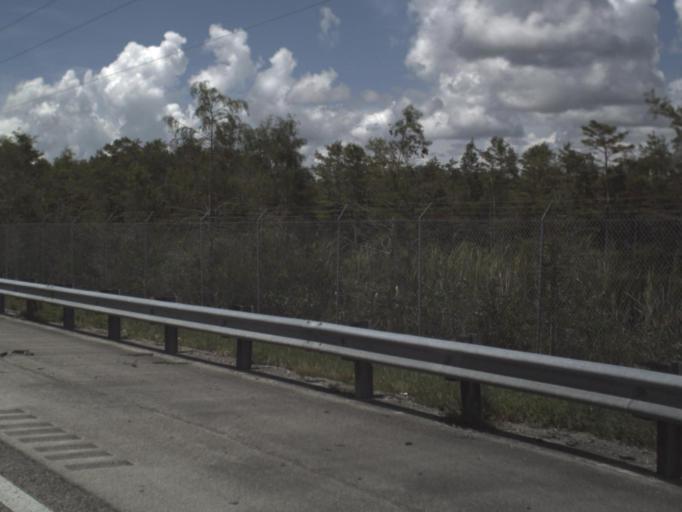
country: US
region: Florida
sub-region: Collier County
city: Immokalee
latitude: 26.1684
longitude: -81.1007
